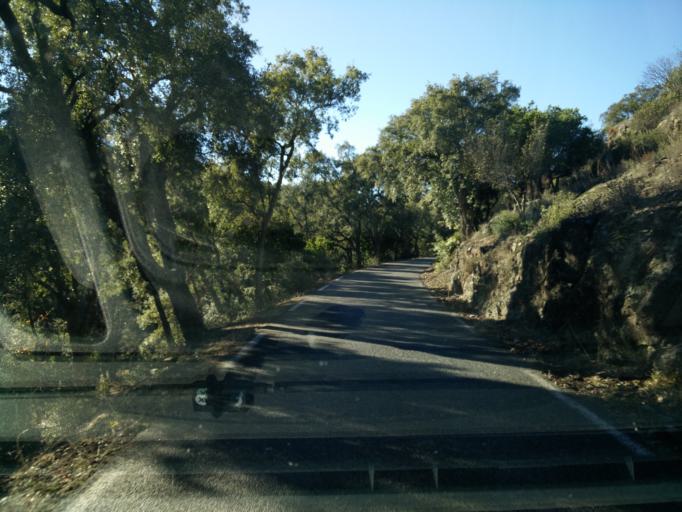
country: FR
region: Provence-Alpes-Cote d'Azur
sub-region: Departement du Var
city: Collobrieres
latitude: 43.2442
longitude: 6.3635
